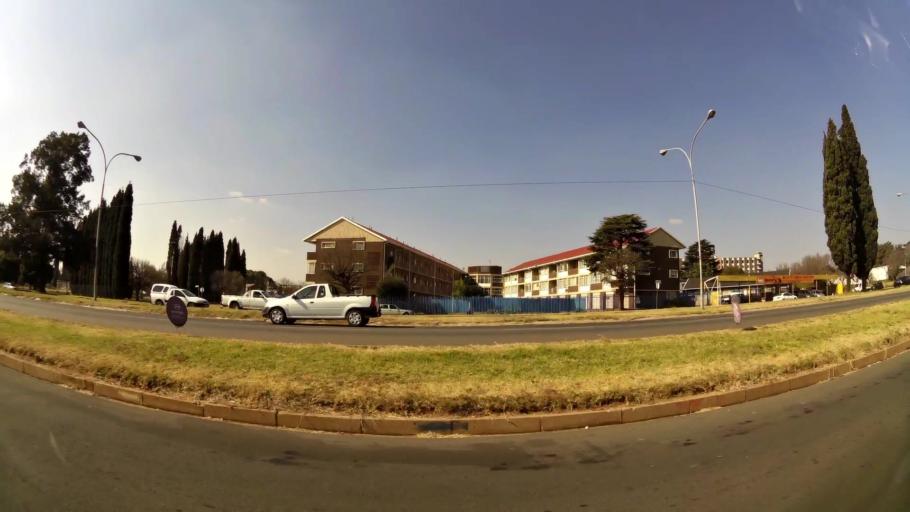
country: ZA
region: Gauteng
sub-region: City of Johannesburg Metropolitan Municipality
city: Modderfontein
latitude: -26.1207
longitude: 28.2283
